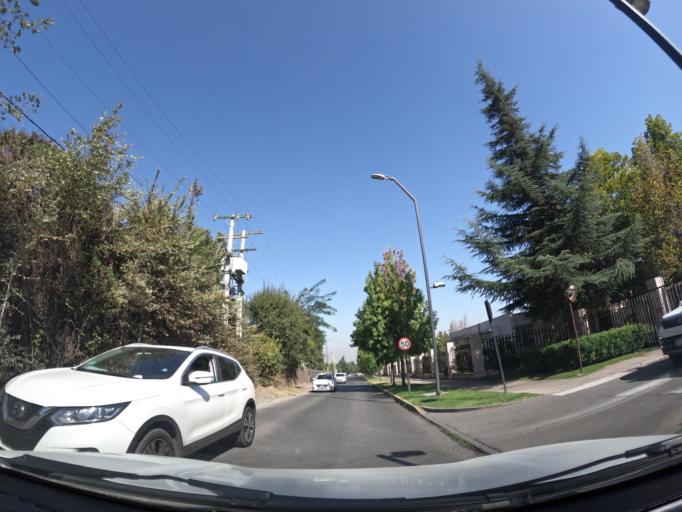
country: CL
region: Santiago Metropolitan
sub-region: Provincia de Santiago
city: Villa Presidente Frei, Nunoa, Santiago, Chile
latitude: -33.5080
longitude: -70.5497
